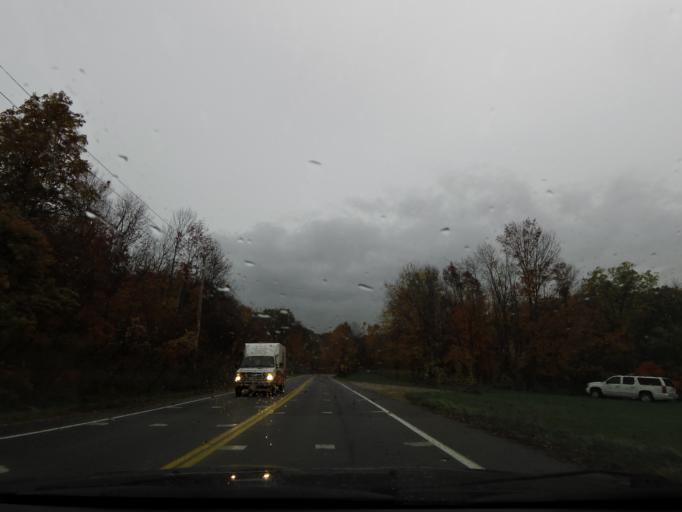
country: CA
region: Ontario
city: Burlington
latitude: 43.4259
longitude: -79.8345
